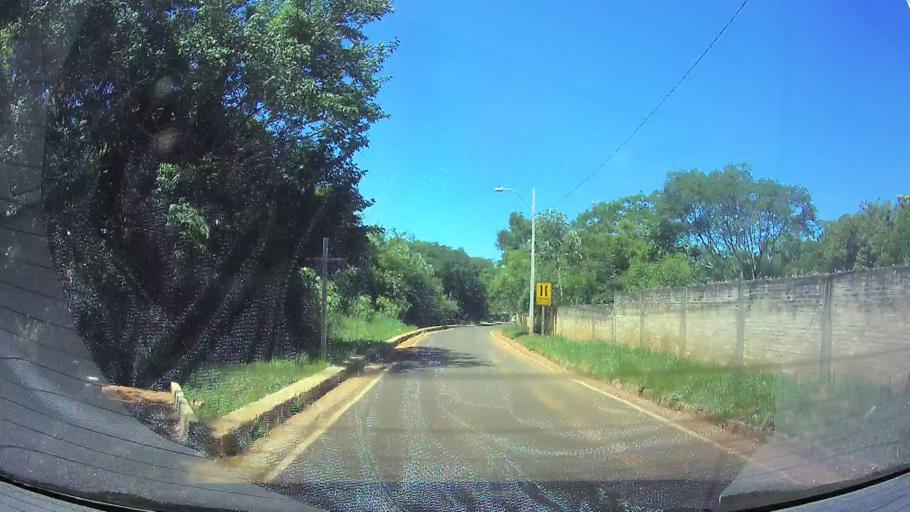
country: PY
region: Central
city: Aregua
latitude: -25.2433
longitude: -57.4372
